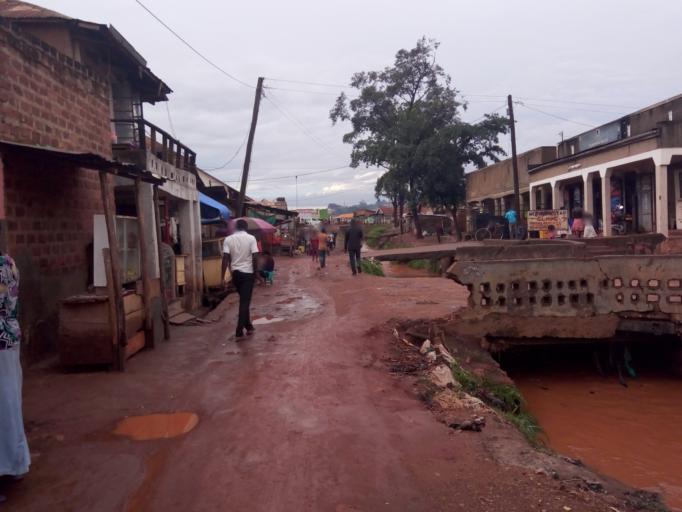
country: UG
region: Central Region
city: Kampala Central Division
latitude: 0.3346
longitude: 32.5596
